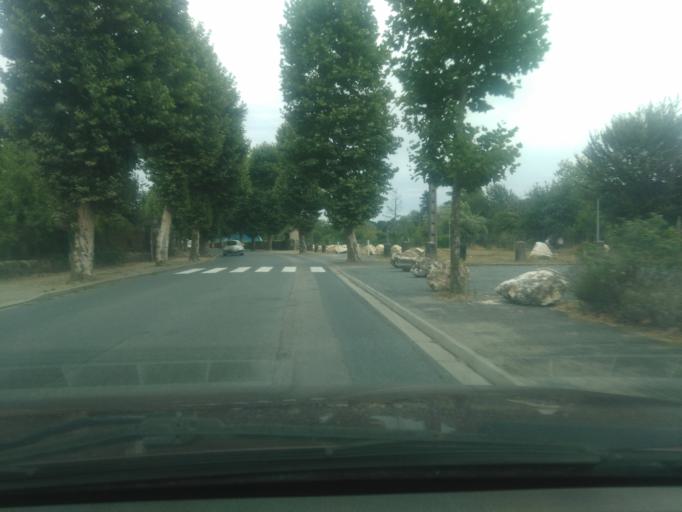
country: FR
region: Centre
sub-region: Departement de l'Indre
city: Le Blanc
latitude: 46.6305
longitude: 1.0649
